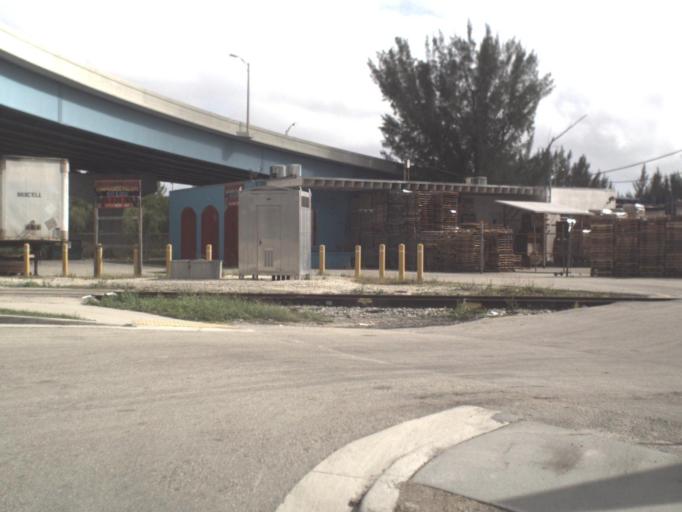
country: US
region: Florida
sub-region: Miami-Dade County
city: Virginia Gardens
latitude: 25.7970
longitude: -80.3089
